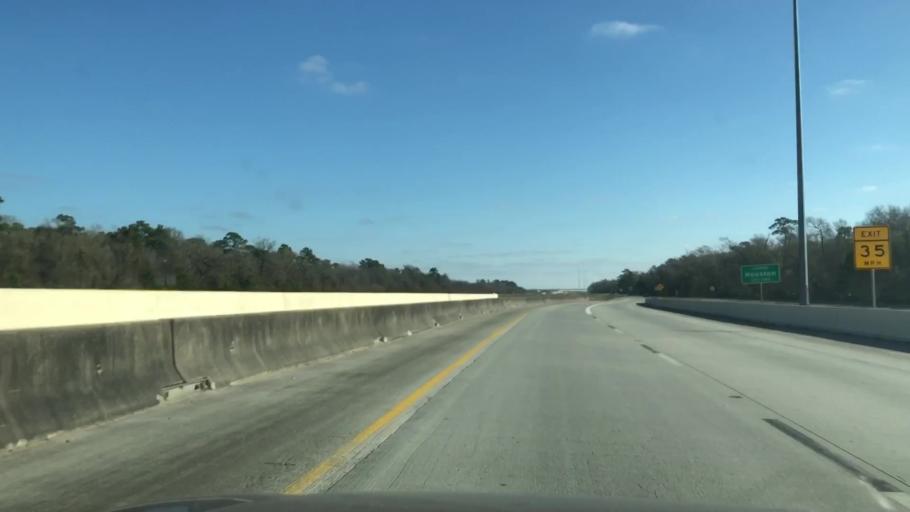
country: US
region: Texas
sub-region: Harris County
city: Cloverleaf
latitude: 29.8203
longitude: -95.2029
